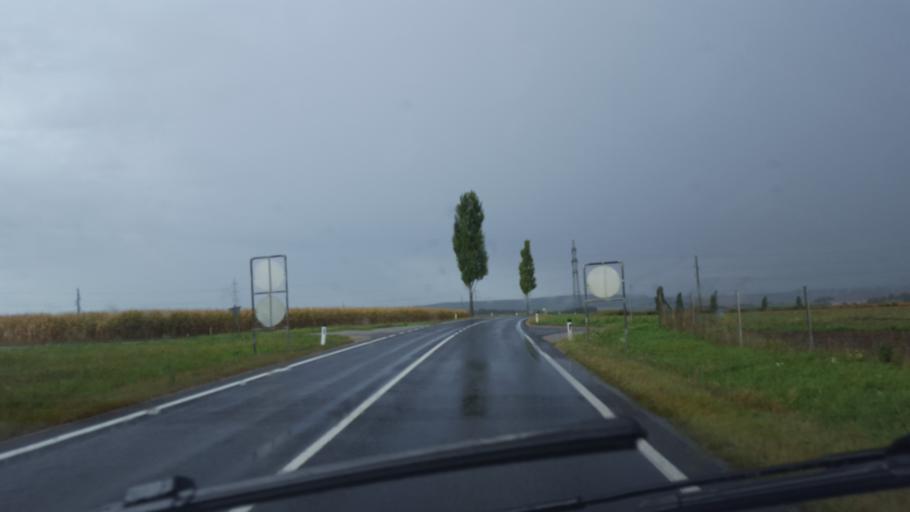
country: AT
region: Lower Austria
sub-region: Politischer Bezirk Bruck an der Leitha
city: Bruck an der Leitha
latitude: 48.0292
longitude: 16.7407
